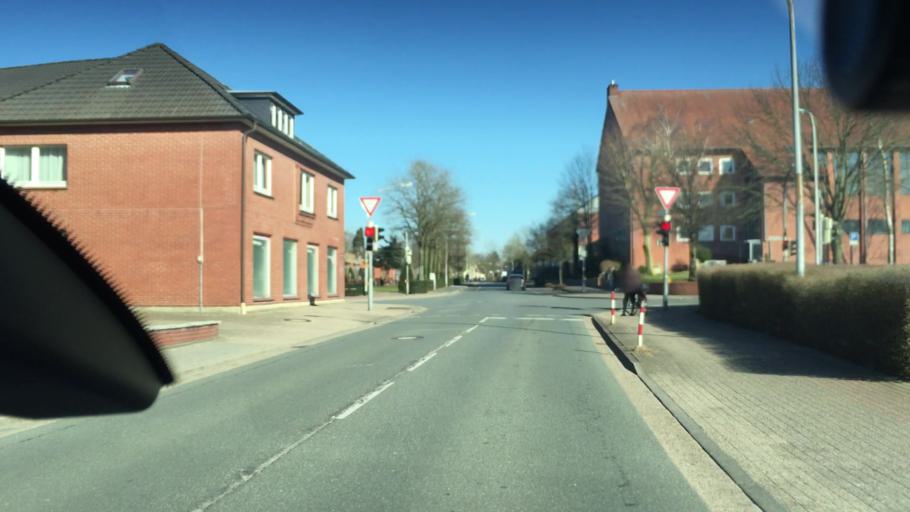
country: DE
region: Lower Saxony
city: Lohne
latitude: 52.6685
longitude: 8.2351
